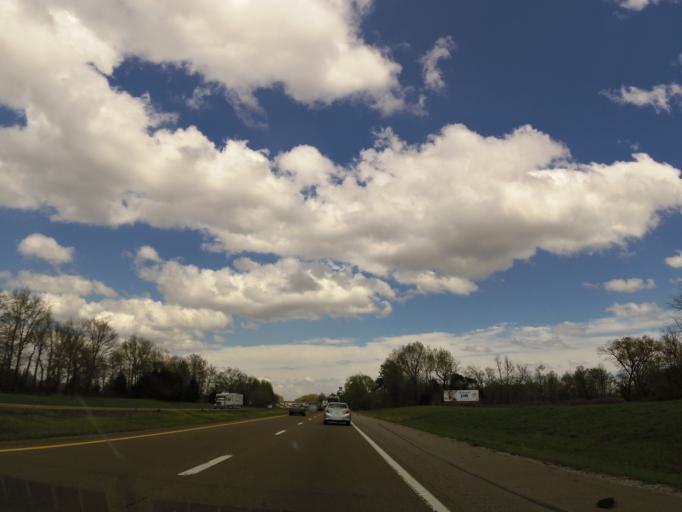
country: US
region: Tennessee
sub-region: Crockett County
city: Bells
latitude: 35.5939
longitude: -89.0632
